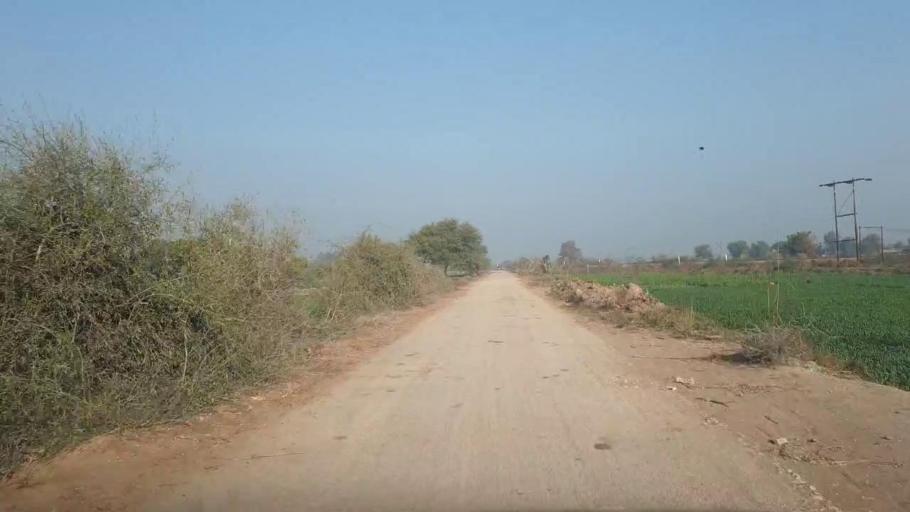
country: PK
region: Sindh
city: Shahdadpur
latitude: 25.9613
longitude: 68.6141
